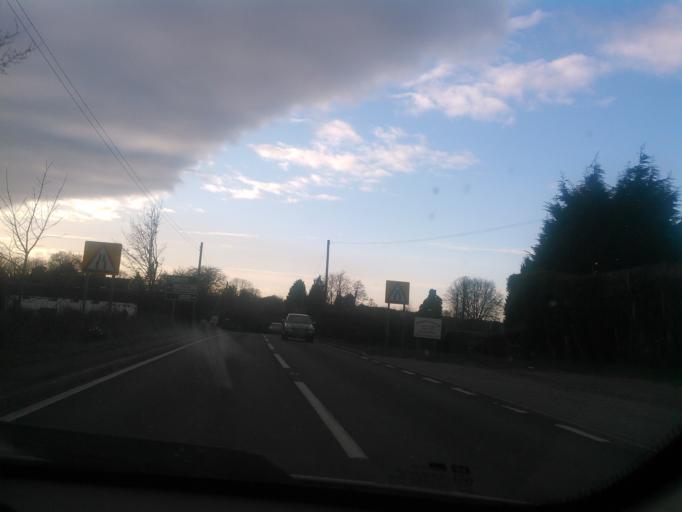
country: GB
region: England
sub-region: Shropshire
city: Stoke upon Tern
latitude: 52.8686
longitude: -2.5078
